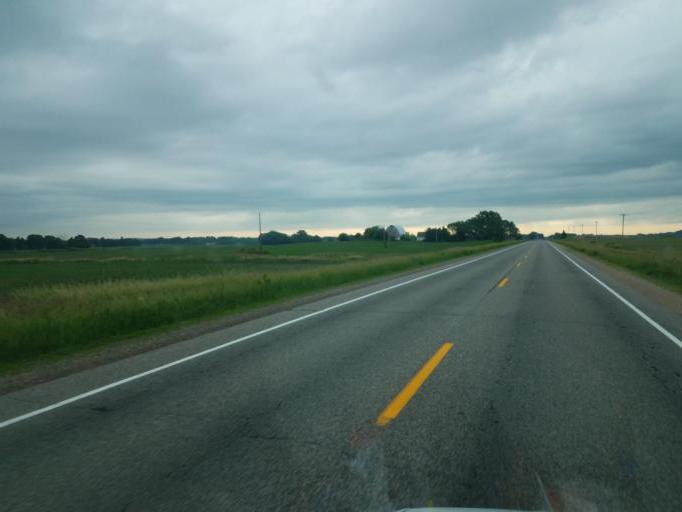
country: US
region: Wisconsin
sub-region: Juneau County
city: Mauston
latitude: 43.7890
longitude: -90.1067
